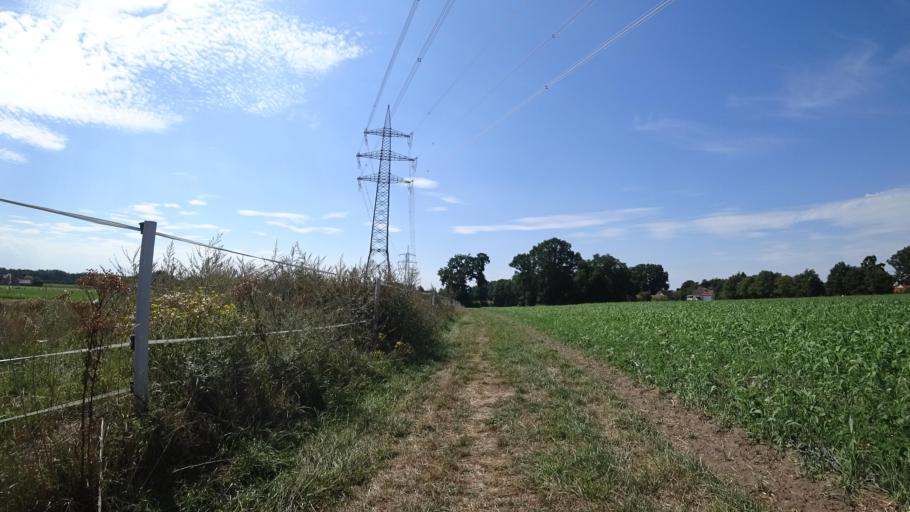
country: DE
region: North Rhine-Westphalia
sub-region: Regierungsbezirk Detmold
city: Steinhagen
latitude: 51.9541
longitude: 8.3920
